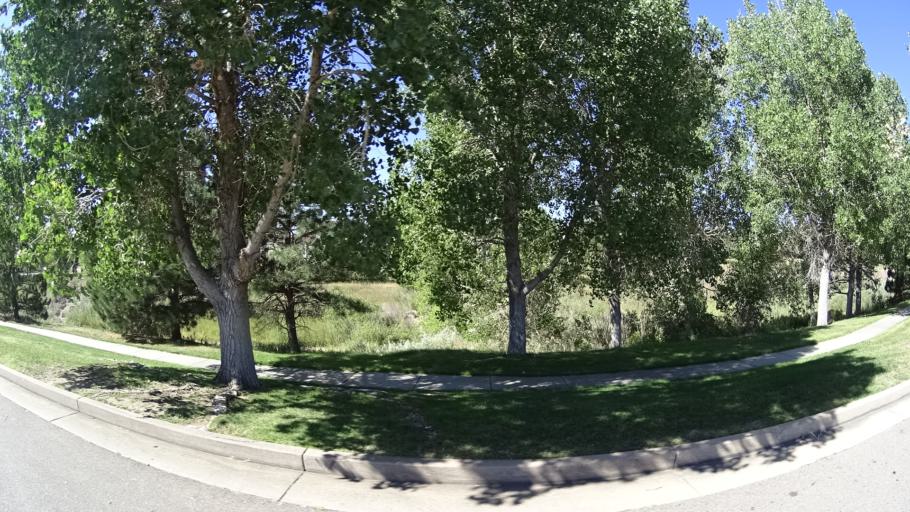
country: US
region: Colorado
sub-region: El Paso County
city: Black Forest
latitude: 38.9544
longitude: -104.7289
